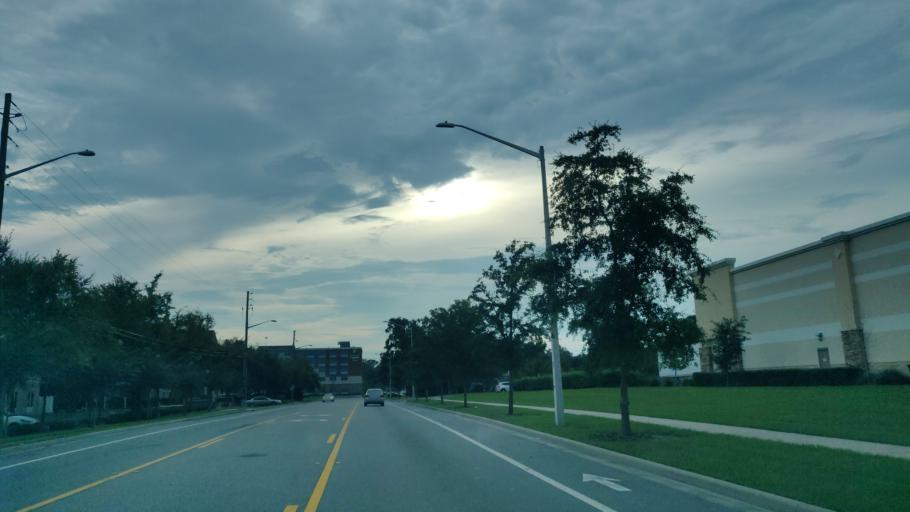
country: US
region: Florida
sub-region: Alachua County
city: Gainesville
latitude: 29.6231
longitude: -82.3846
